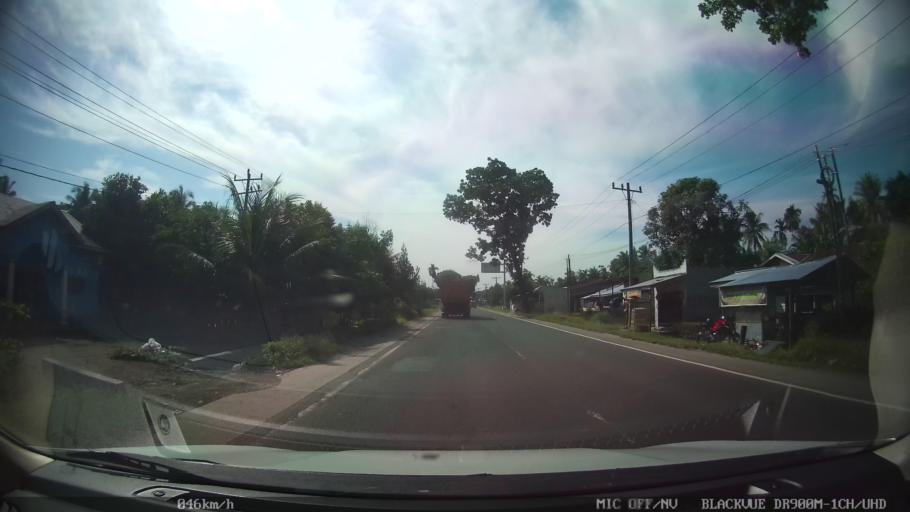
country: ID
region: North Sumatra
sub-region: Kabupaten Langkat
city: Stabat
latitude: 3.7270
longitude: 98.4973
